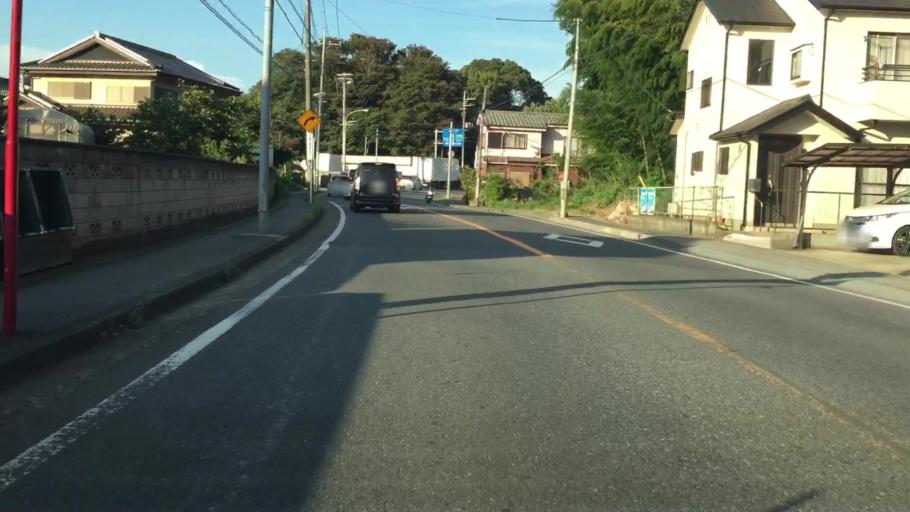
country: JP
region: Chiba
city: Funabashi
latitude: 35.7299
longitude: 140.0003
